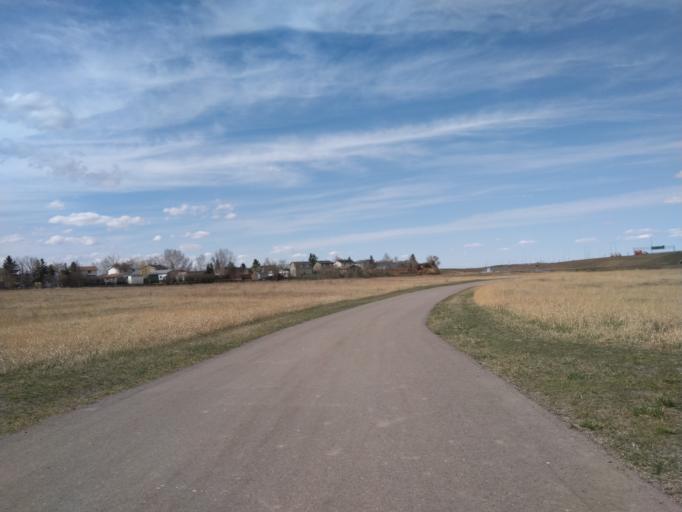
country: CA
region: Alberta
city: Chestermere
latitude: 51.0526
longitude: -113.9236
